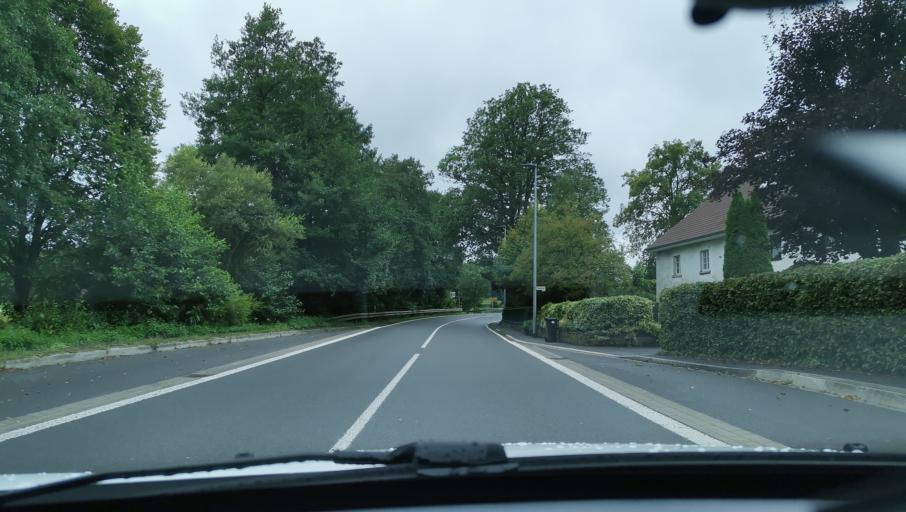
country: DE
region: North Rhine-Westphalia
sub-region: Regierungsbezirk Arnsberg
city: Schalksmuhle
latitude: 51.2087
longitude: 7.5389
